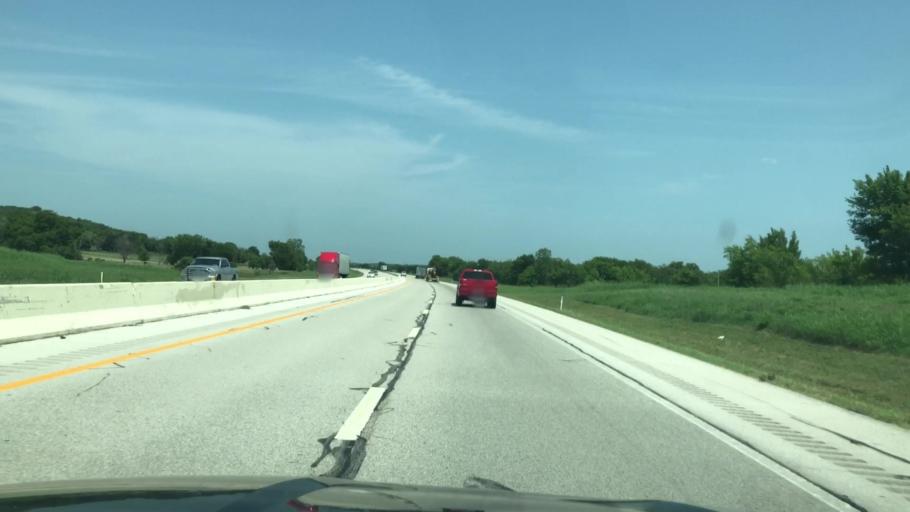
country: US
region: Oklahoma
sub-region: Rogers County
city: Justice
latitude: 36.3483
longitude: -95.4687
